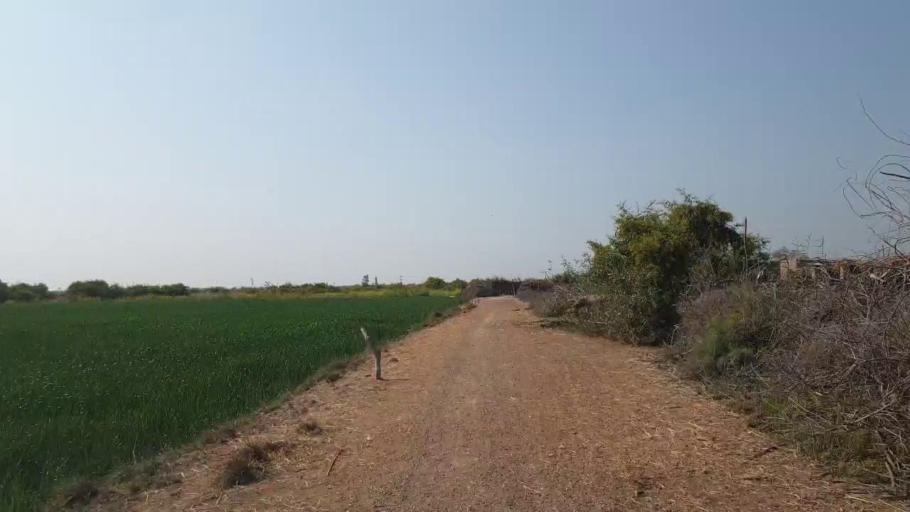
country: PK
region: Sindh
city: Bhit Shah
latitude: 25.9409
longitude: 68.4800
